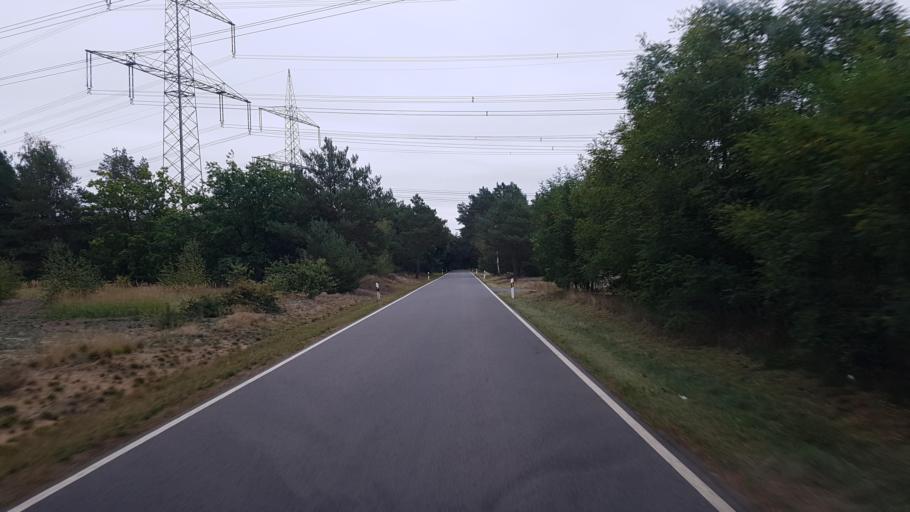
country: DE
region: Brandenburg
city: Luckau
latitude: 51.8793
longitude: 13.6835
